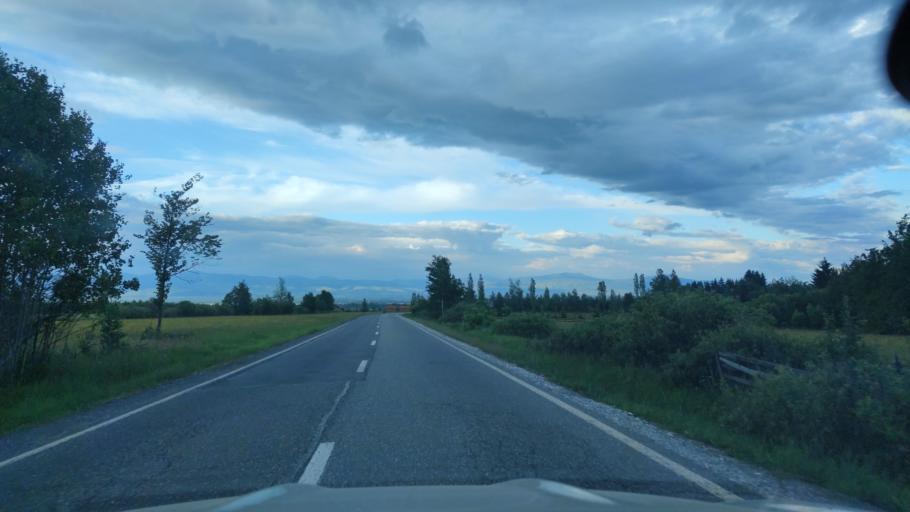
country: RO
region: Harghita
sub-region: Comuna Joseni
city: Joseni
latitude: 46.6766
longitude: 25.3844
